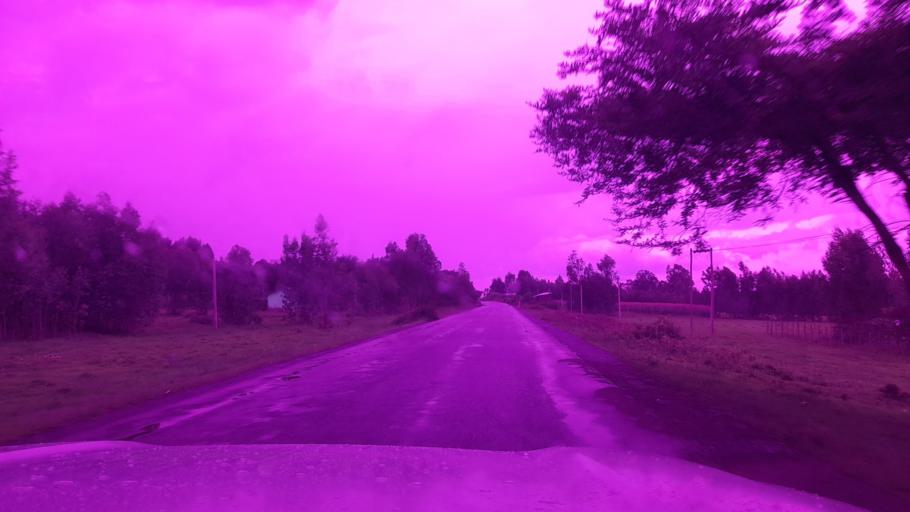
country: ET
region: Oromiya
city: Jima
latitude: 7.7069
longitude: 37.0724
